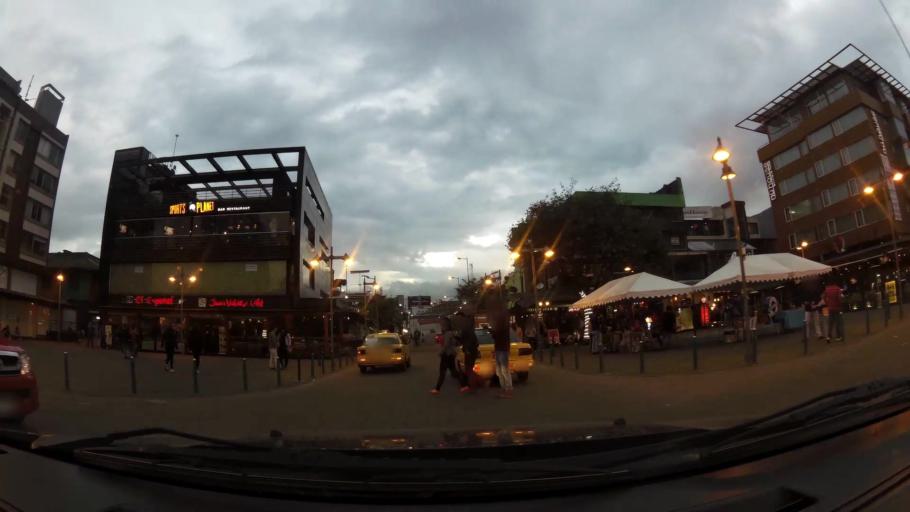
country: EC
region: Pichincha
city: Quito
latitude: -0.2029
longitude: -78.4910
